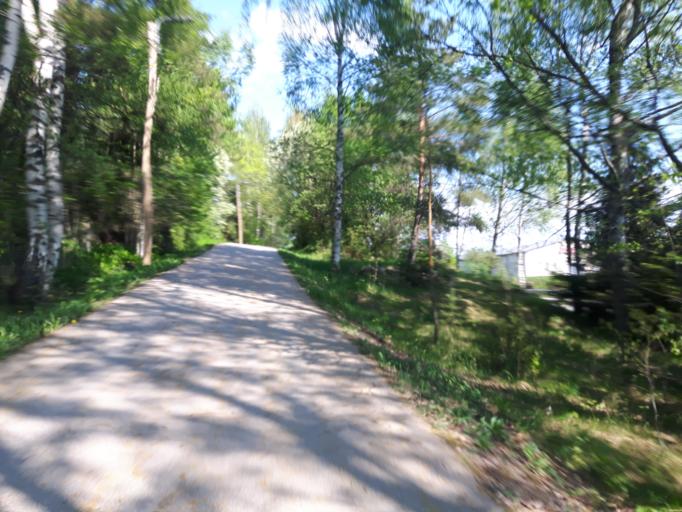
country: FI
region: Uusimaa
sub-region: Porvoo
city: Porvoo
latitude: 60.3802
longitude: 25.6167
